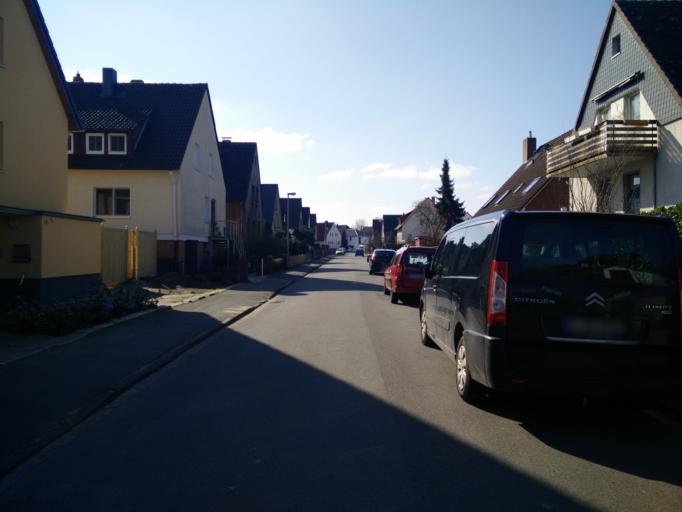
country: DE
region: Lower Saxony
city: Langenhagen
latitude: 52.4298
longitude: 9.7266
